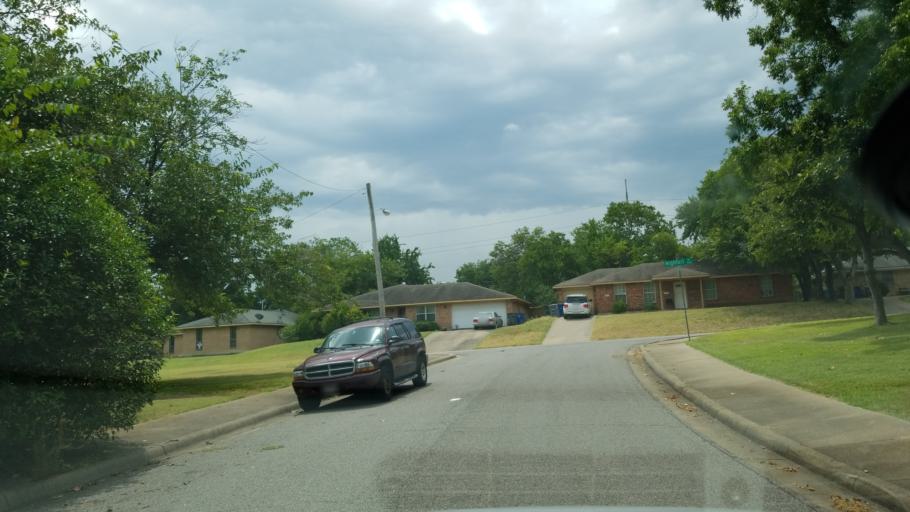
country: US
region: Texas
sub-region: Dallas County
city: Duncanville
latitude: 32.6631
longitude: -96.8353
